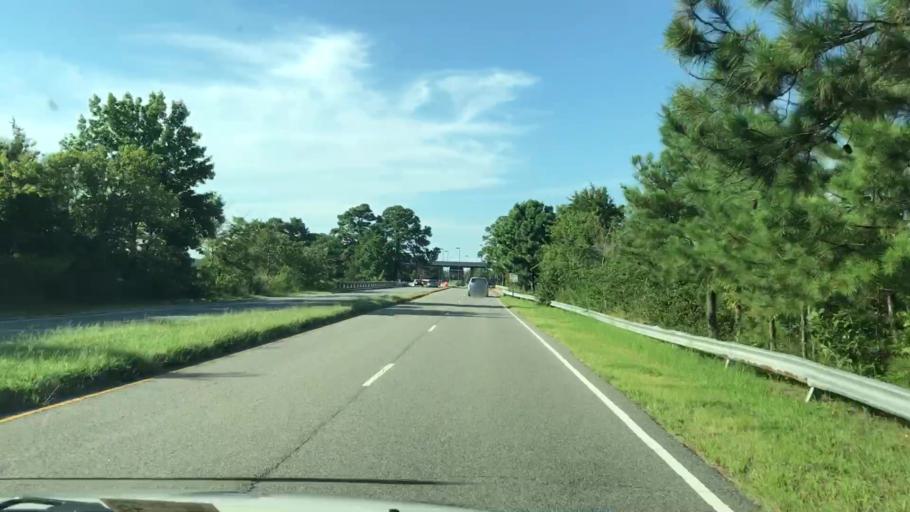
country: US
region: Virginia
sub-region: City of Hampton
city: Hampton
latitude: 37.0628
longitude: -76.3658
